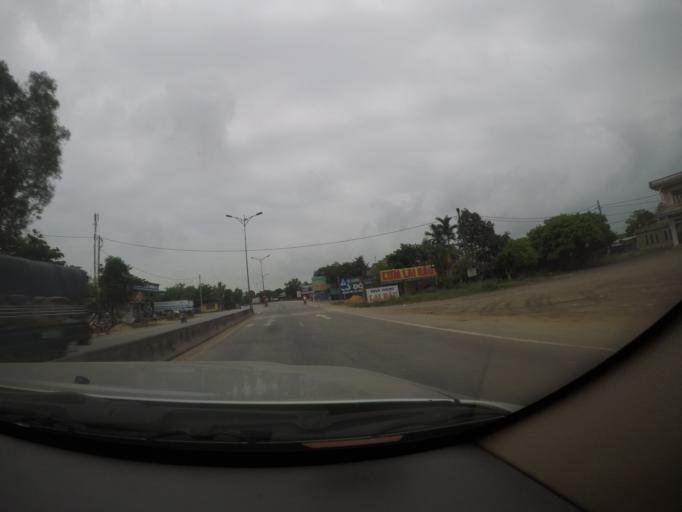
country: VN
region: Thua Thien-Hue
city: Phong Dien
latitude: 16.6033
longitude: 107.3273
